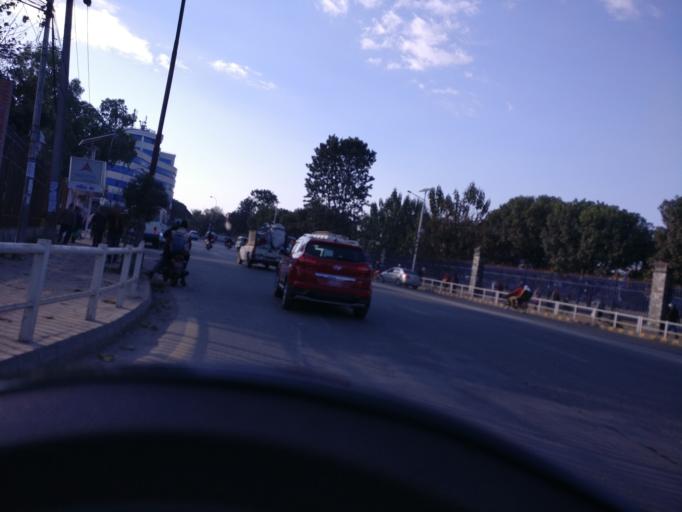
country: NP
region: Central Region
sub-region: Bagmati Zone
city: Kathmandu
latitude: 27.6995
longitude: 85.3147
